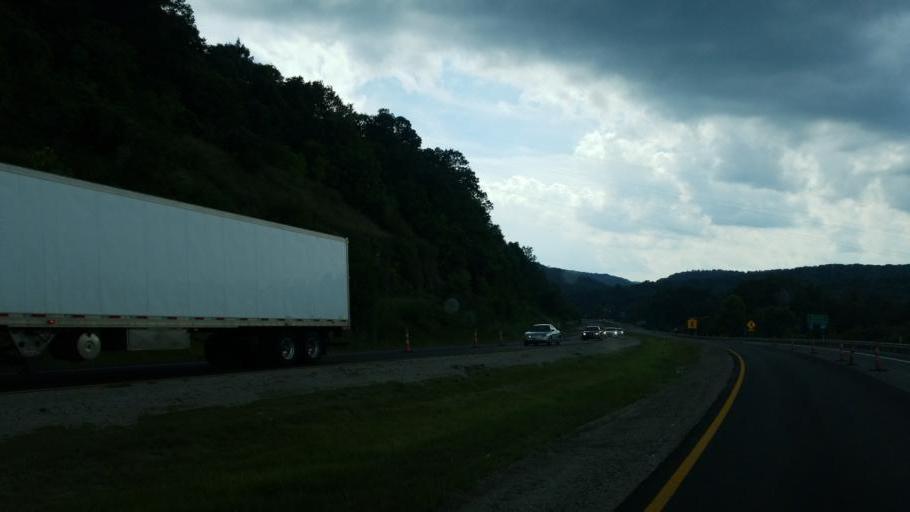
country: US
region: West Virginia
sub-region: Kanawha County
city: Alum Creek
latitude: 38.2680
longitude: -81.8249
